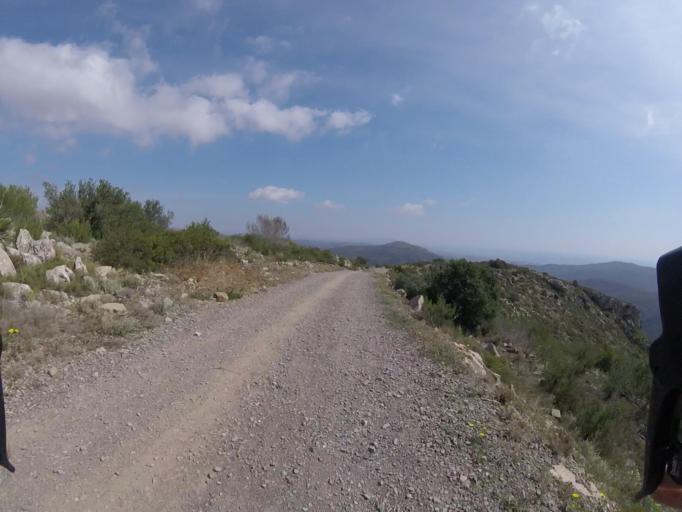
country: ES
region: Valencia
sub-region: Provincia de Castello
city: Benicassim
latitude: 40.0959
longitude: 0.0475
